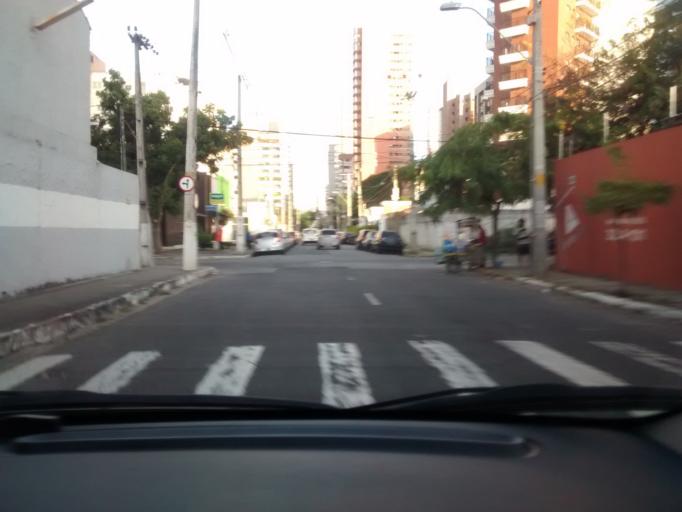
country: BR
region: Ceara
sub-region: Fortaleza
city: Fortaleza
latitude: -3.7395
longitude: -38.4953
